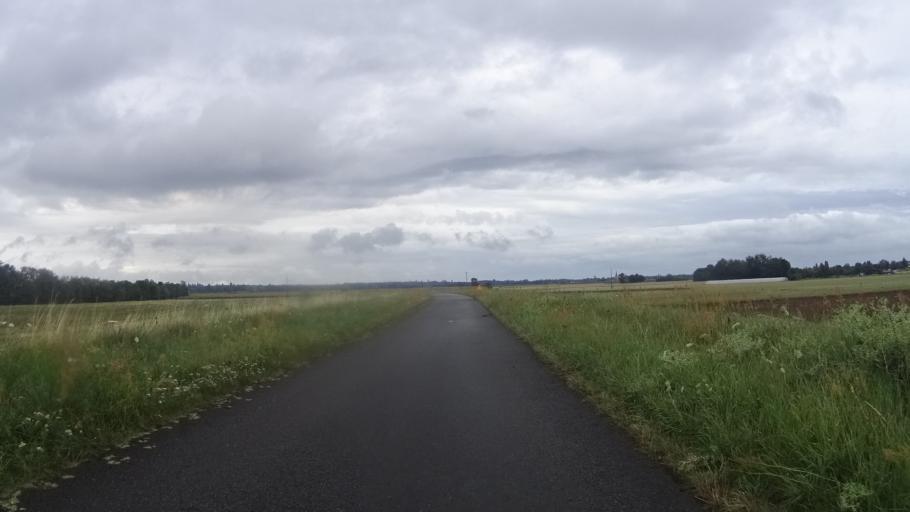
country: FR
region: Centre
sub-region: Departement du Loiret
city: Mardie
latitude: 47.8580
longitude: 2.0683
